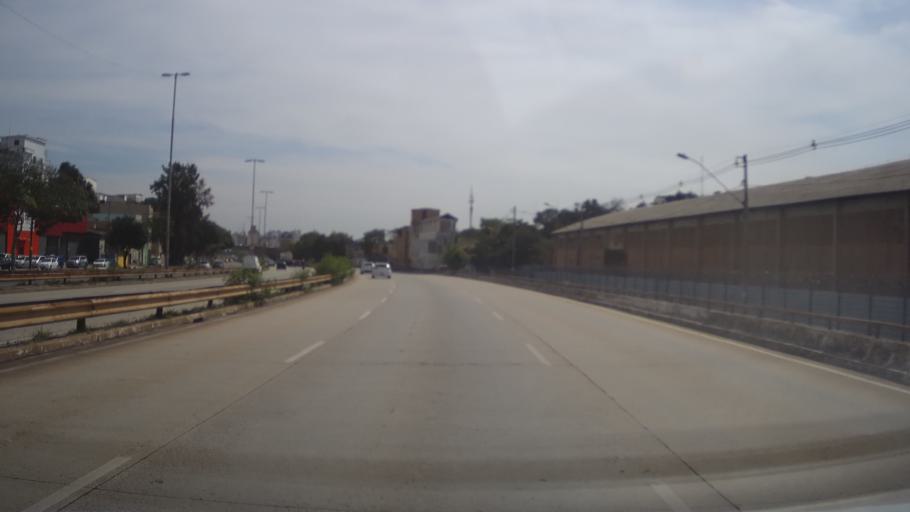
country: BR
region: Minas Gerais
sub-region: Contagem
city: Contagem
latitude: -19.9356
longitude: -43.9969
